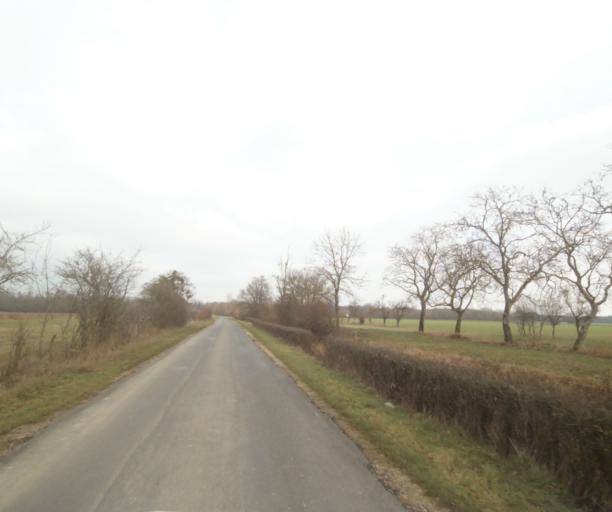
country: FR
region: Champagne-Ardenne
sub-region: Departement de la Haute-Marne
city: Villiers-en-Lieu
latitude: 48.6599
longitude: 4.8294
